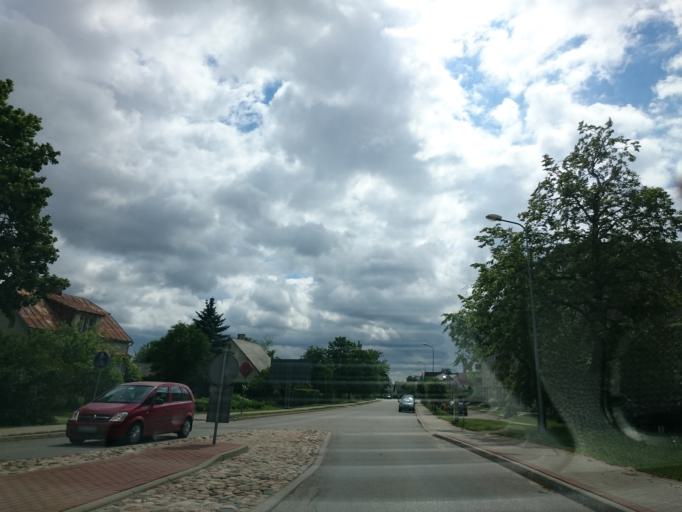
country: LV
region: Madonas Rajons
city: Madona
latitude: 56.8579
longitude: 26.2048
